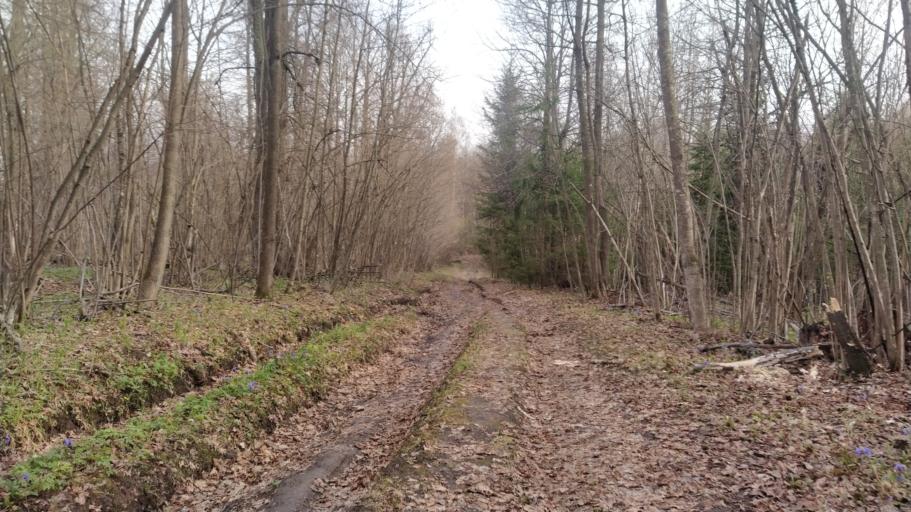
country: RU
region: Chuvashia
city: Novyye Lapsary
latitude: 56.1325
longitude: 47.1221
